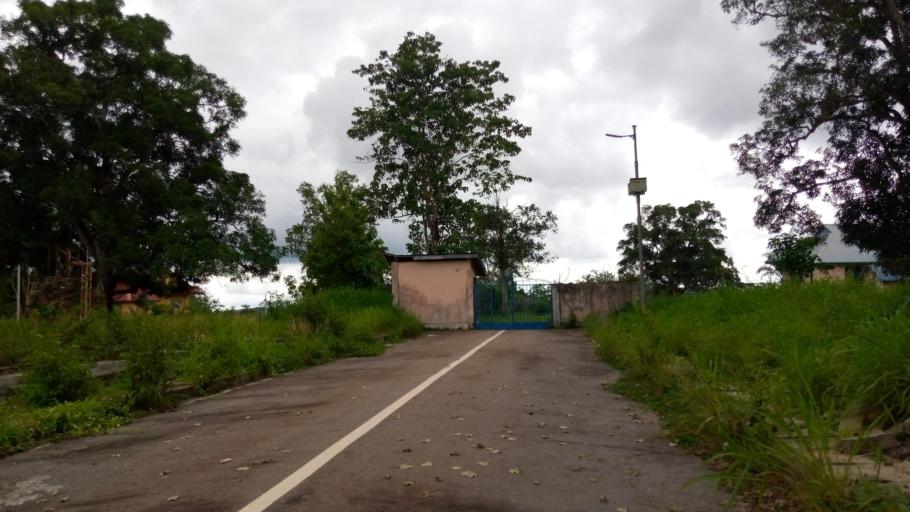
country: SL
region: Southern Province
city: Moyamba
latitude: 8.1600
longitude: -12.4446
